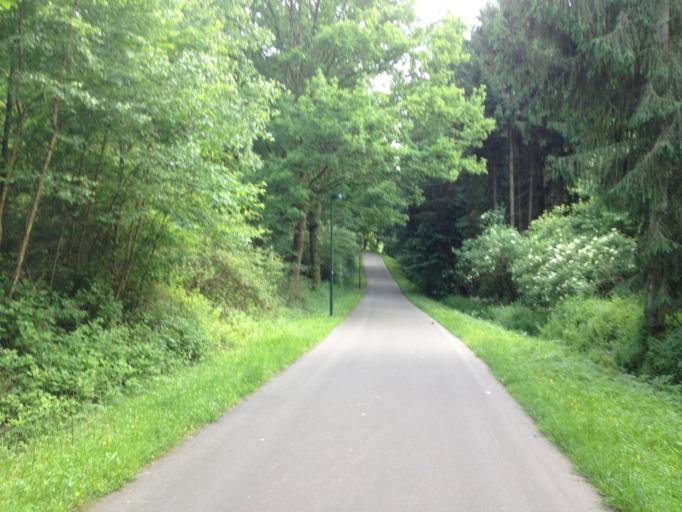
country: DE
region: Saarland
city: Namborn
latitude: 49.4729
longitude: 7.1200
